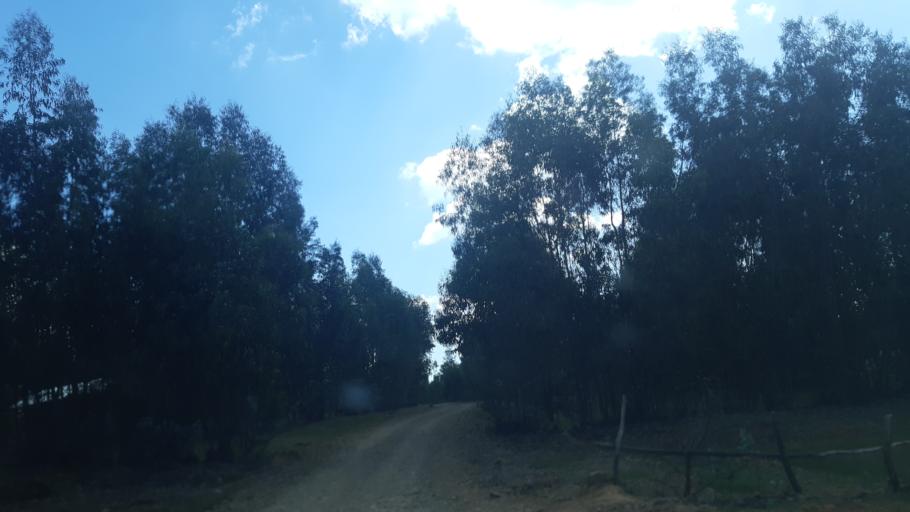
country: ET
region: Amhara
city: Dabat
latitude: 13.3564
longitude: 37.3854
